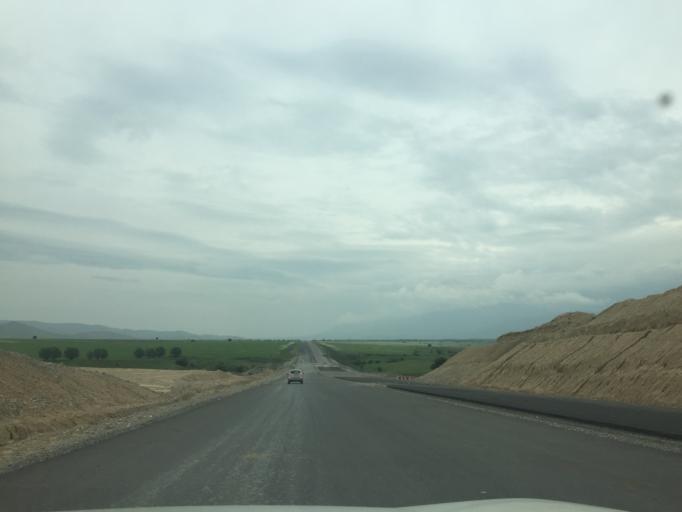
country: KZ
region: Ongtustik Qazaqstan
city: Turar Ryskulov
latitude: 42.5081
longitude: 70.4105
